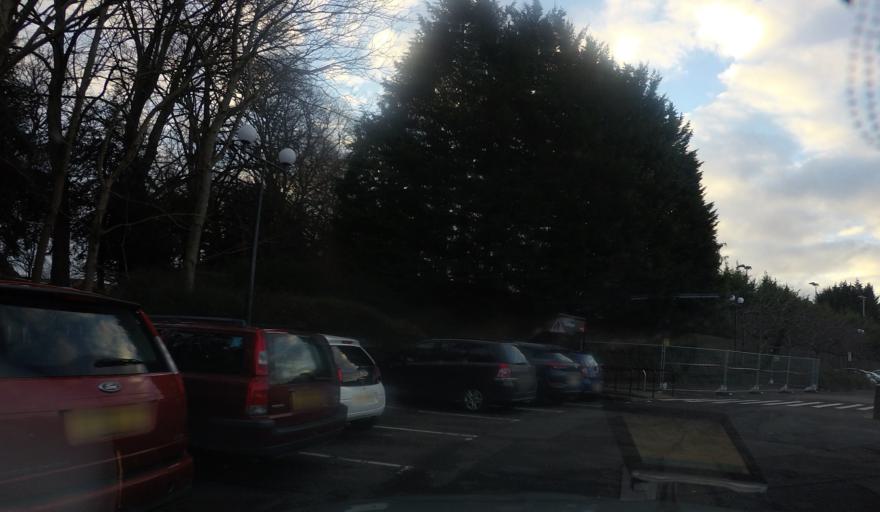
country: GB
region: Scotland
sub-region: Edinburgh
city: Edinburgh
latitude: 55.9252
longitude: -3.1634
